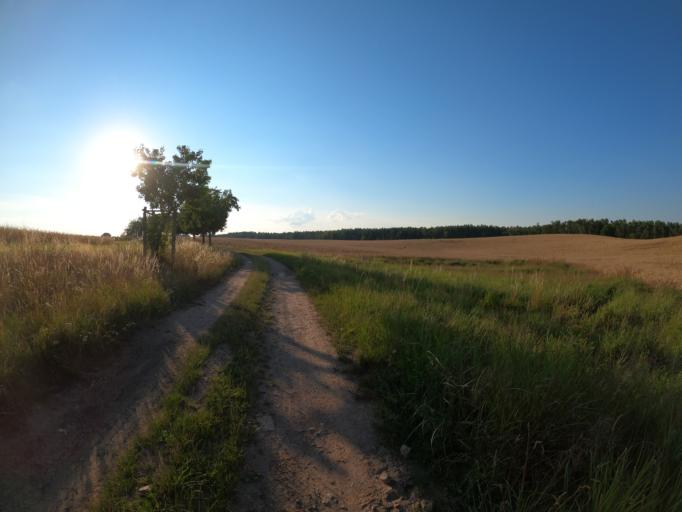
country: DE
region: Brandenburg
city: Althuttendorf
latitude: 53.0343
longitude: 13.8743
